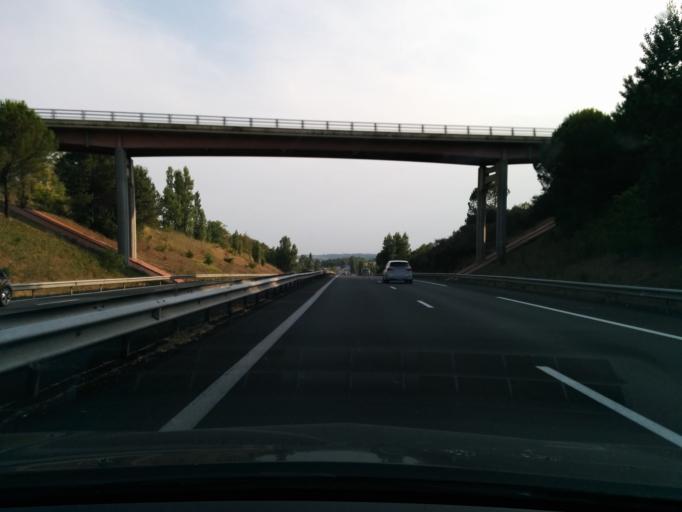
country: FR
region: Midi-Pyrenees
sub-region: Departement de la Haute-Garonne
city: Garidech
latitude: 43.7250
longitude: 1.5709
